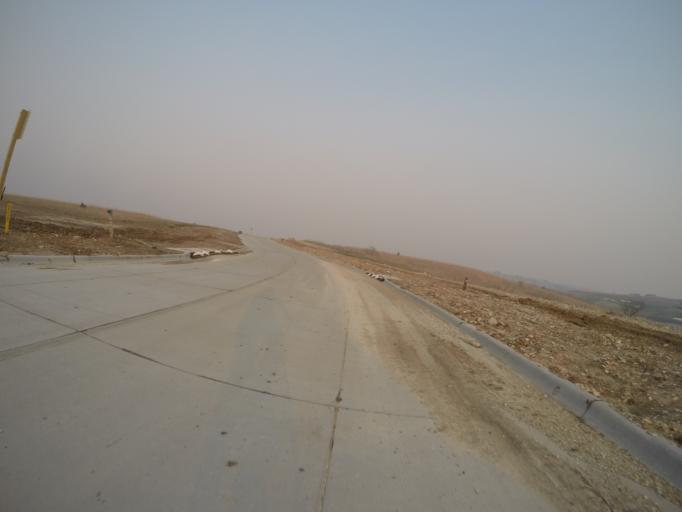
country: US
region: Kansas
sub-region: Riley County
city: Manhattan
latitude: 39.2180
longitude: -96.6410
